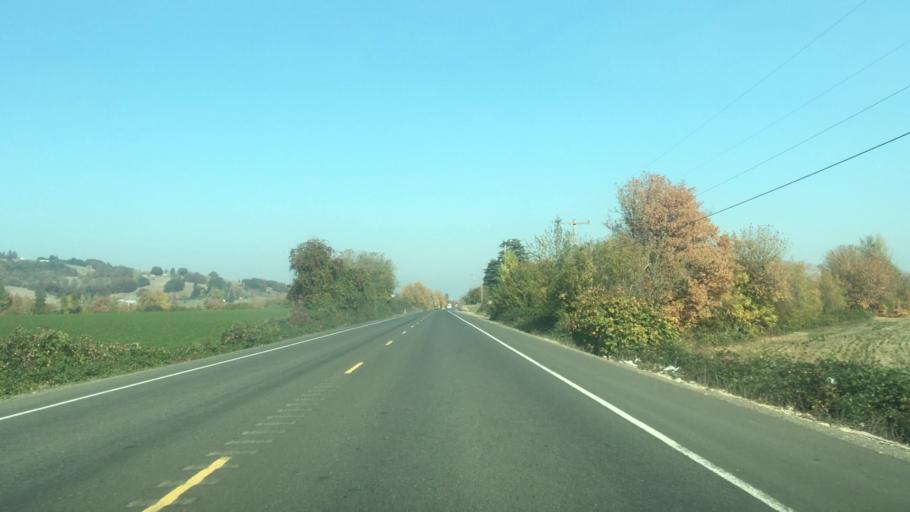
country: US
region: Oregon
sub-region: Yamhill County
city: Sheridan
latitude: 45.1237
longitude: -123.3070
